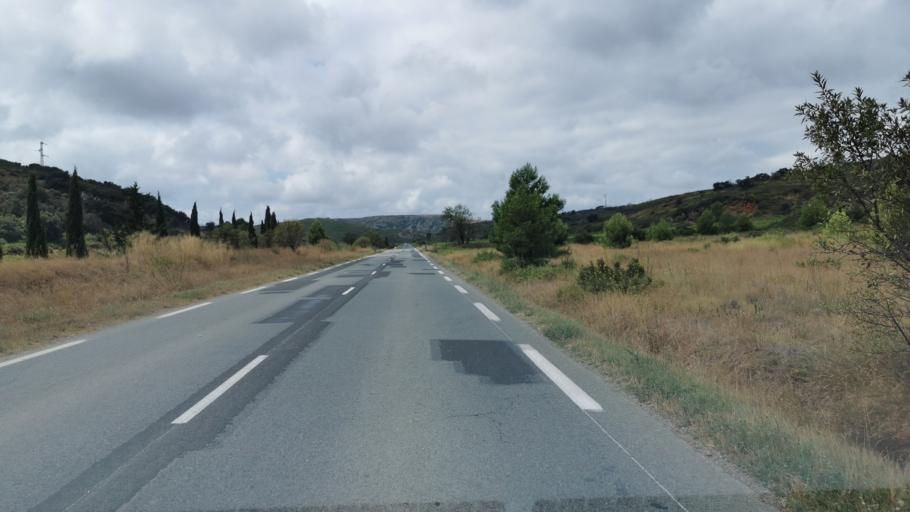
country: FR
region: Languedoc-Roussillon
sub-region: Departement de l'Aude
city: Nevian
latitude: 43.1757
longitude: 2.9305
